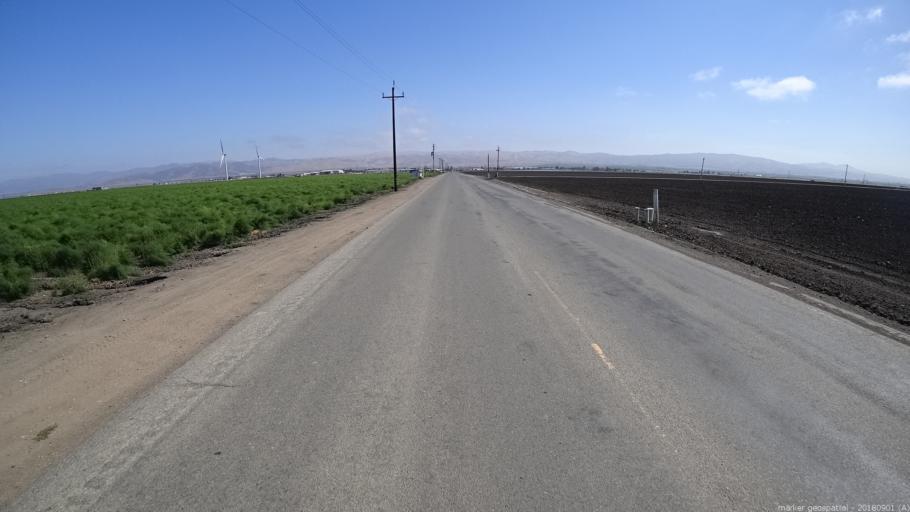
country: US
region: California
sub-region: Monterey County
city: Gonzales
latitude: 36.4932
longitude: -121.4578
